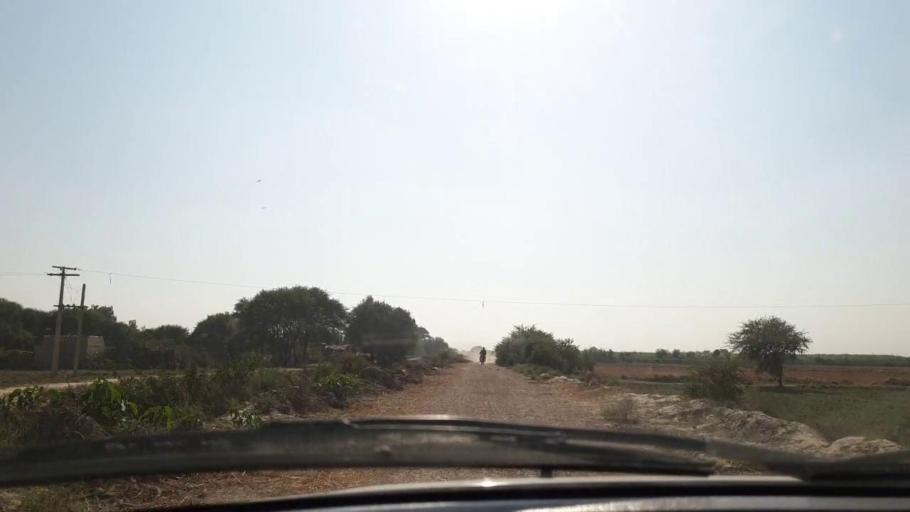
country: PK
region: Sindh
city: Bulri
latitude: 24.8430
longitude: 68.3329
